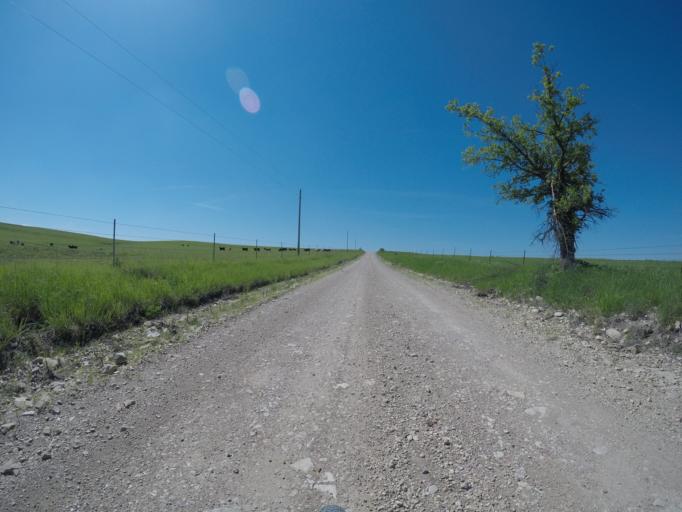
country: US
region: Kansas
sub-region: Wabaunsee County
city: Alma
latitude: 39.0035
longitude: -96.1783
